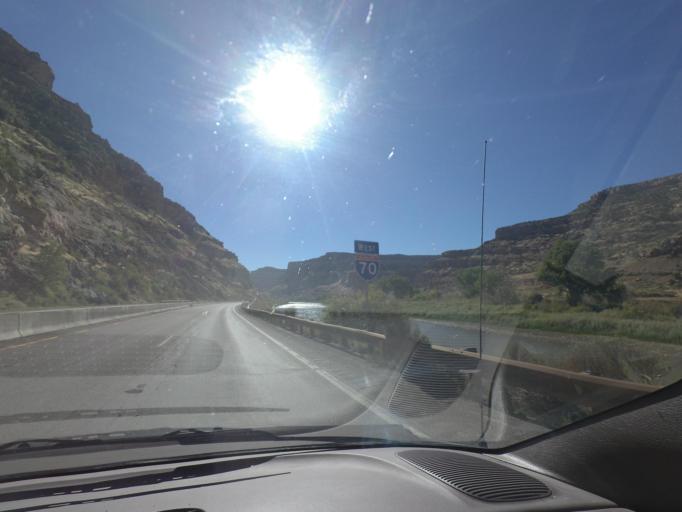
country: US
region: Colorado
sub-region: Mesa County
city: Palisade
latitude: 39.1788
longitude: -108.2862
